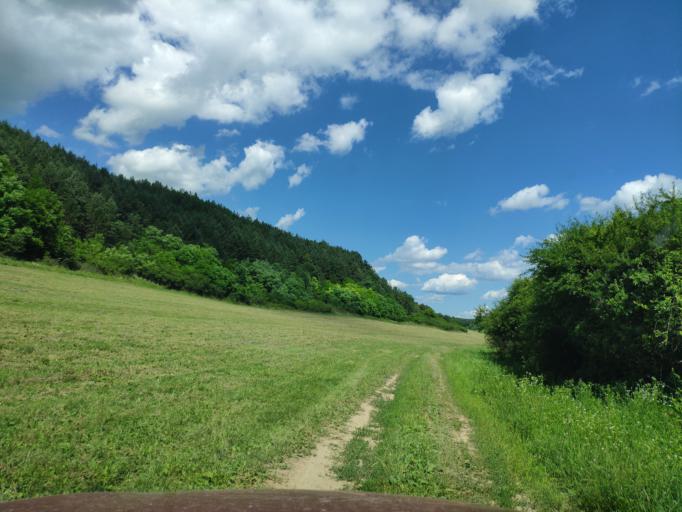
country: HU
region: Borsod-Abauj-Zemplen
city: Arlo
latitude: 48.2700
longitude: 20.1895
